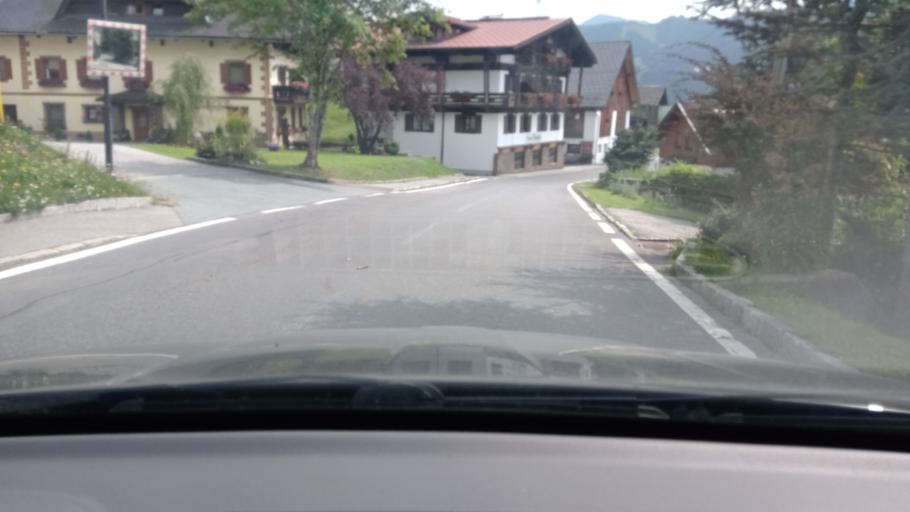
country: AT
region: Carinthia
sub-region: Politischer Bezirk Spittal an der Drau
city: Steinfeld
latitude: 46.7231
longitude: 13.2741
